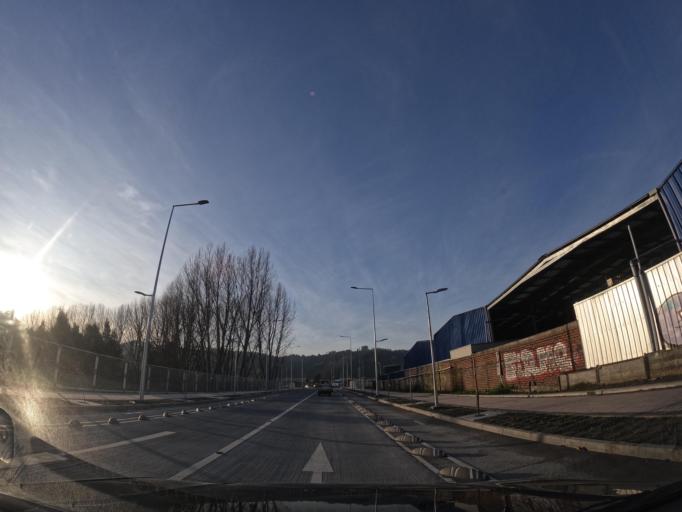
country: CL
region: Biobio
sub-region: Provincia de Concepcion
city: Concepcion
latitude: -36.8202
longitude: -73.0082
